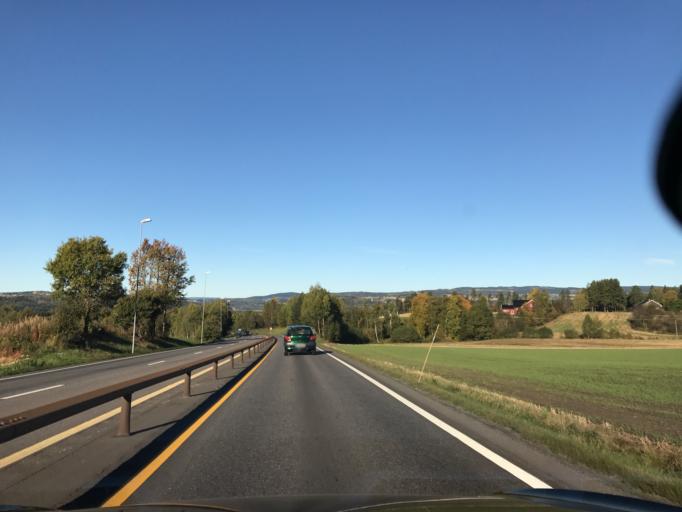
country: NO
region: Hedmark
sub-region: Ringsaker
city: Brumunddal
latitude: 60.8589
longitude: 10.9730
